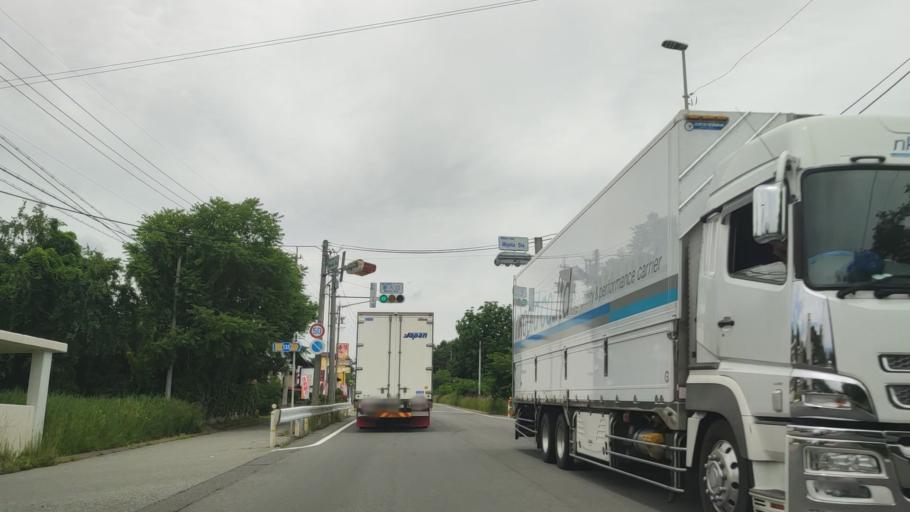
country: JP
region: Nagano
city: Komoro
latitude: 36.3215
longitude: 138.4985
